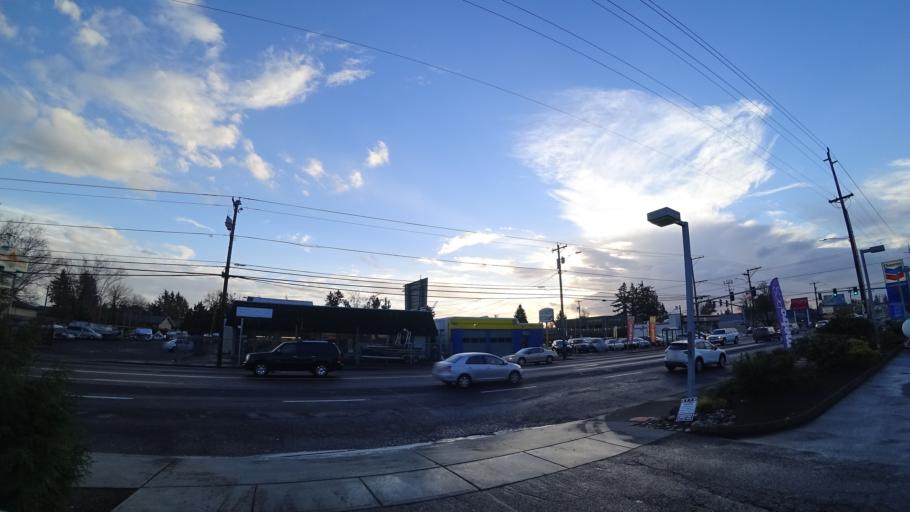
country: US
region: Oregon
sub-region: Multnomah County
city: Lents
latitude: 45.5193
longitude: -122.5099
